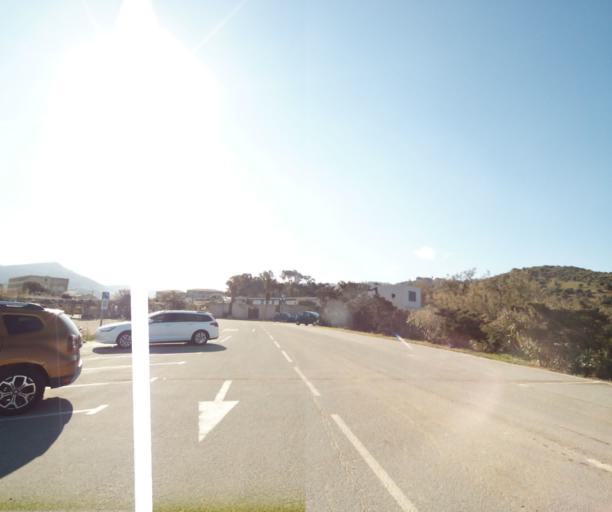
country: FR
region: Corsica
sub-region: Departement de la Corse-du-Sud
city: Propriano
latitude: 41.6751
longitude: 8.8943
